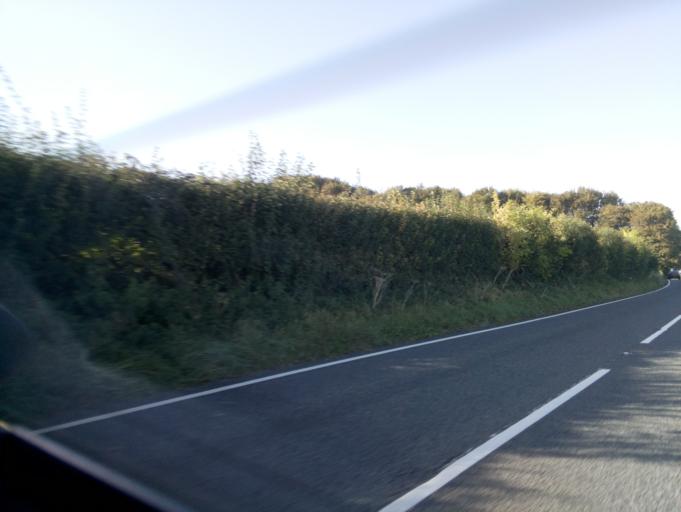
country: GB
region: England
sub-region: Hampshire
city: Swanmore
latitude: 50.9381
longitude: -1.1411
